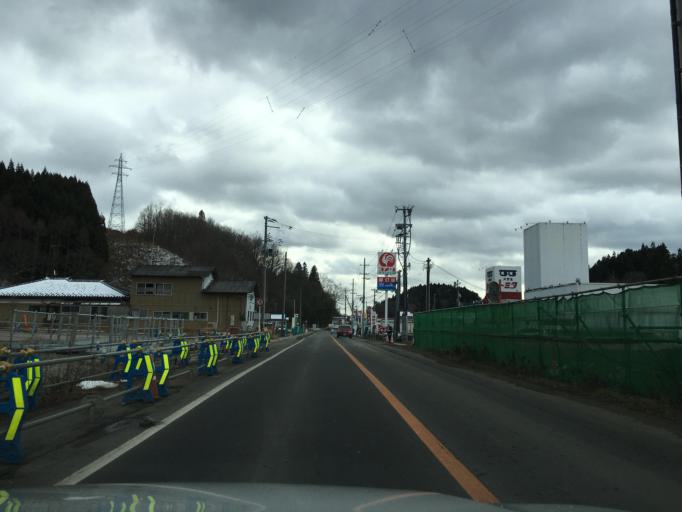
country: JP
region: Fukushima
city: Funehikimachi-funehiki
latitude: 37.2964
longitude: 140.6207
